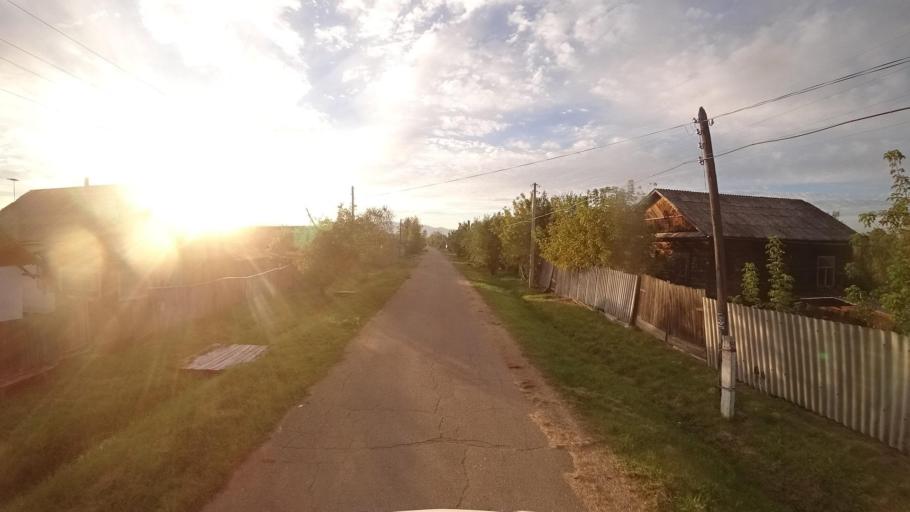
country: RU
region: Primorskiy
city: Yakovlevka
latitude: 44.4241
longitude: 133.4879
